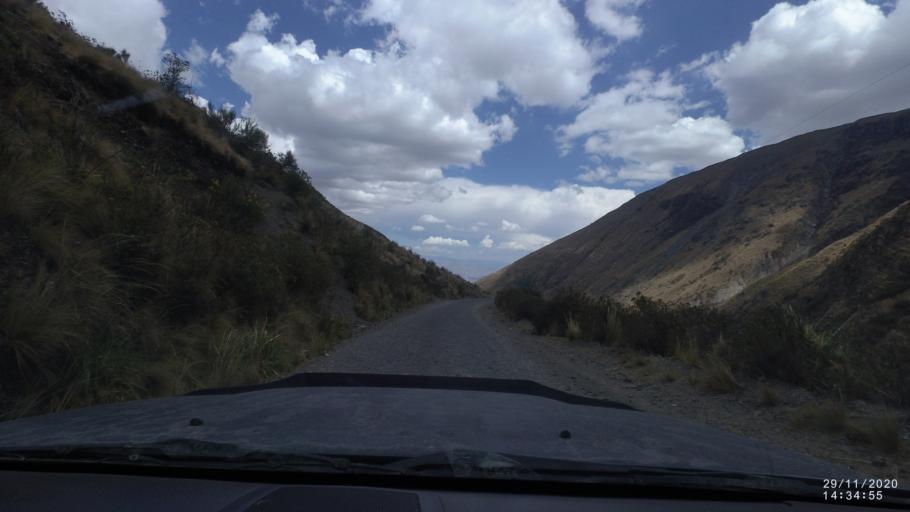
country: BO
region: Cochabamba
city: Sipe Sipe
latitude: -17.2687
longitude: -66.3403
